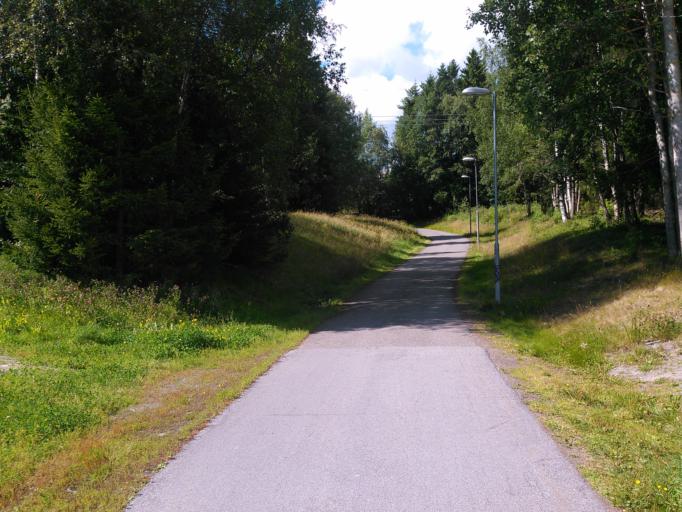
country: SE
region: Vaesterbotten
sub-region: Umea Kommun
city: Ersmark
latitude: 63.8307
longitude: 20.3160
